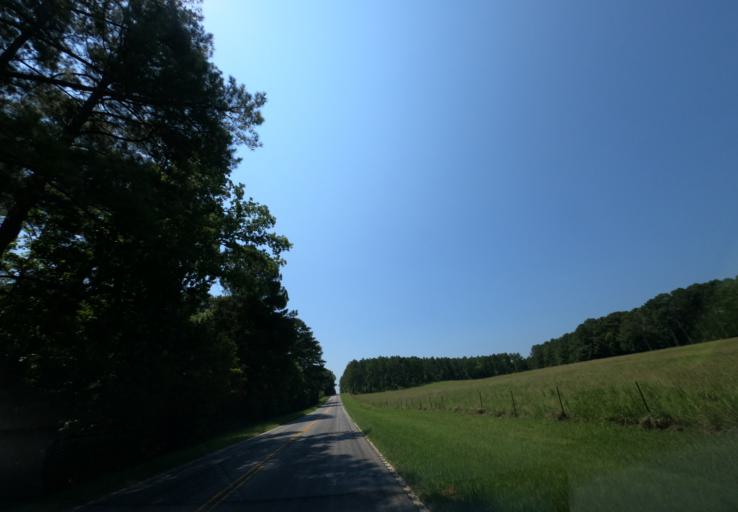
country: US
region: South Carolina
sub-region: McCormick County
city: McCormick
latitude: 33.9800
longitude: -82.1297
